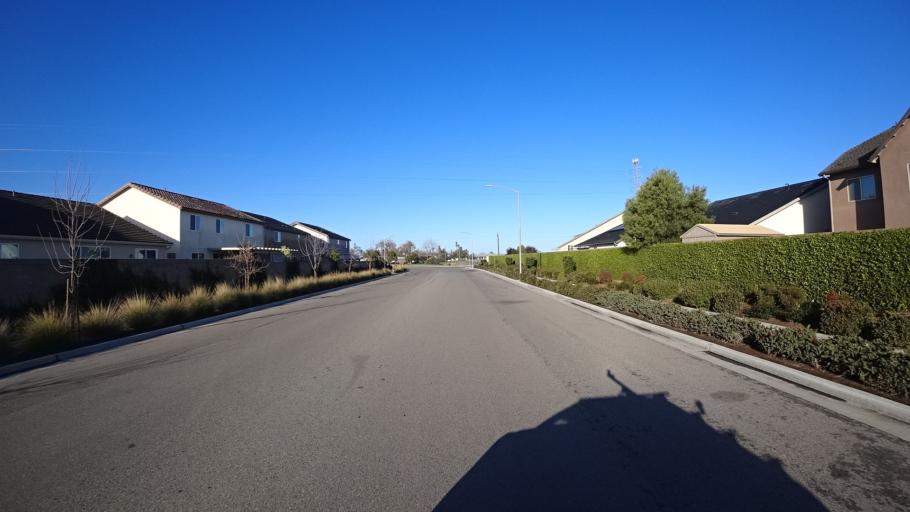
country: US
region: California
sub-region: Fresno County
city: Biola
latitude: 36.8397
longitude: -119.9139
